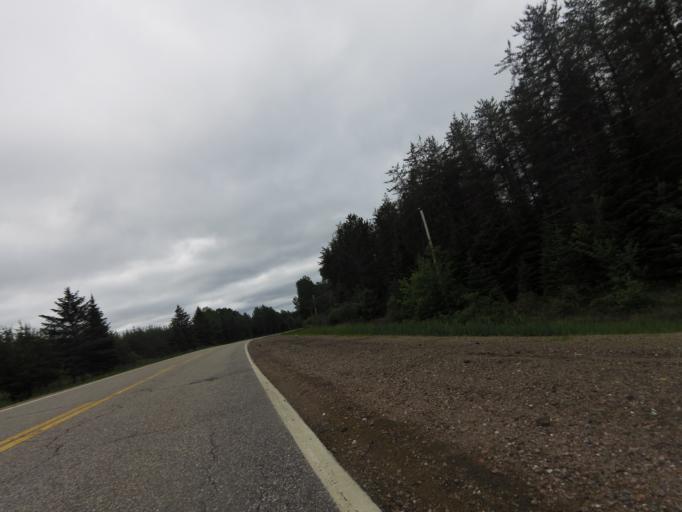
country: CA
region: Quebec
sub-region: Outaouais
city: Shawville
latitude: 45.8795
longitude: -76.3993
